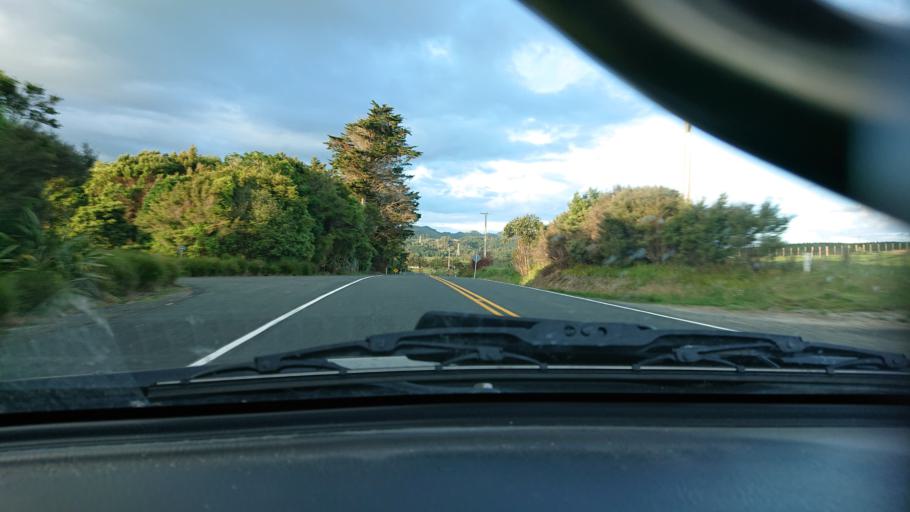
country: NZ
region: Auckland
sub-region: Auckland
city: Parakai
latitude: -36.5201
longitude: 174.4490
